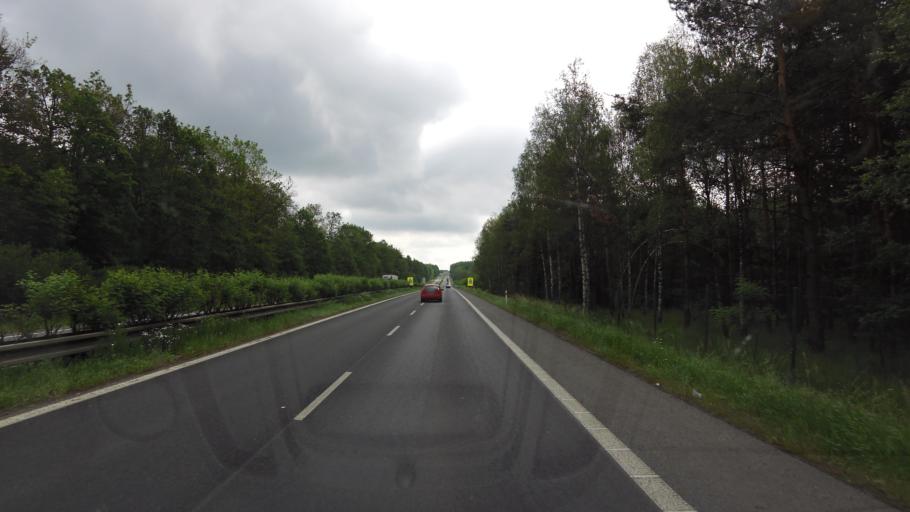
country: CZ
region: Plzensky
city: Dysina
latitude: 49.7463
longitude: 13.4546
